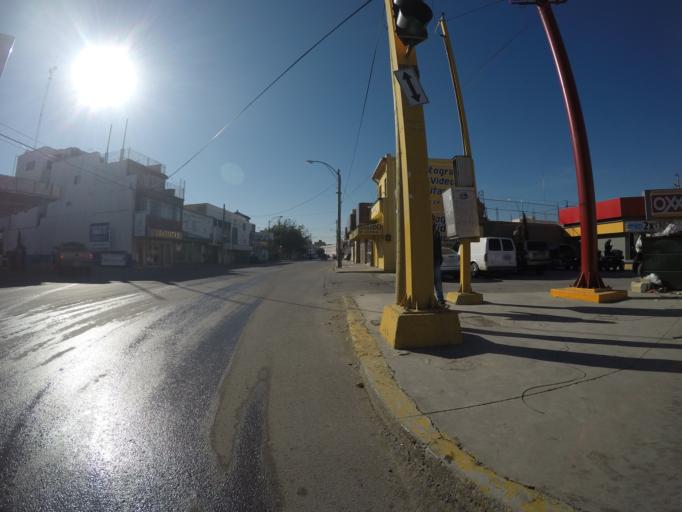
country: MX
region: Chihuahua
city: Ciudad Juarez
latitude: 31.7430
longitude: -106.4814
